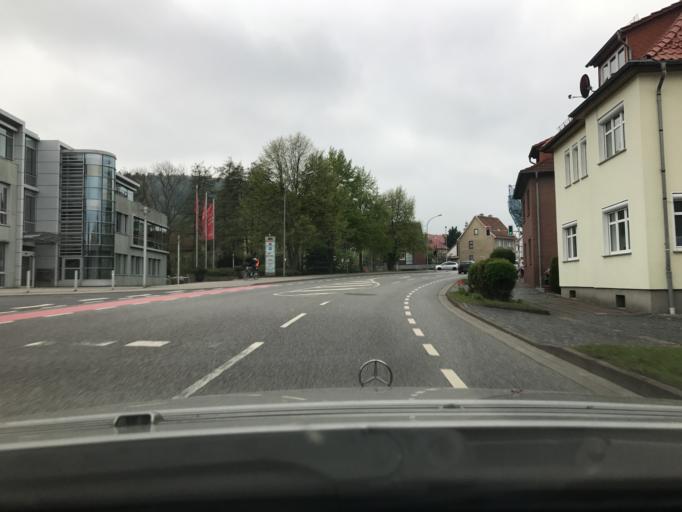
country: DE
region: Thuringia
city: Heilbad Heiligenstadt
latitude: 51.3761
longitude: 10.1432
